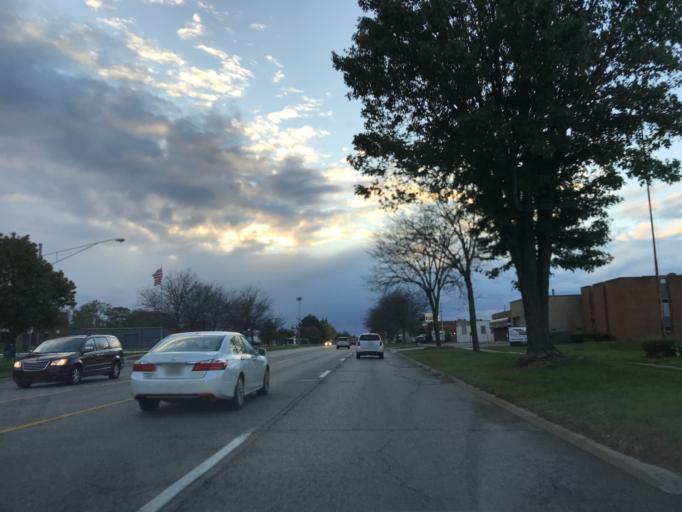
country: US
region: Michigan
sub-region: Oakland County
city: Farmington
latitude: 42.4409
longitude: -83.3649
